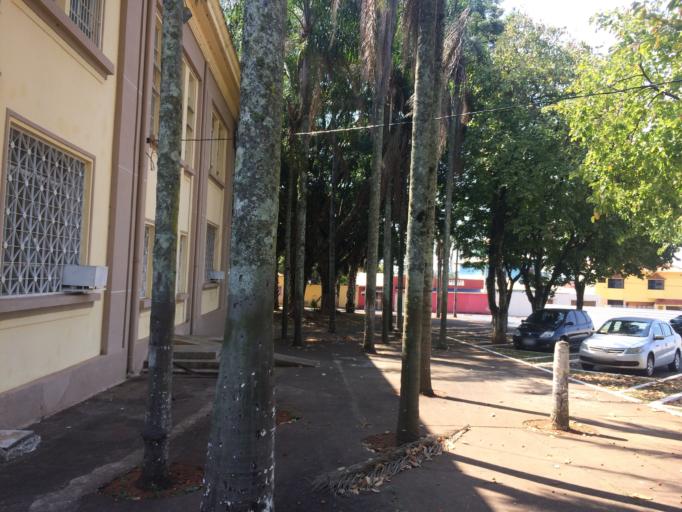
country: BR
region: Sao Paulo
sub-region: Capao Bonito
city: Capao Bonito
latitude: -24.0021
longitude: -48.3462
